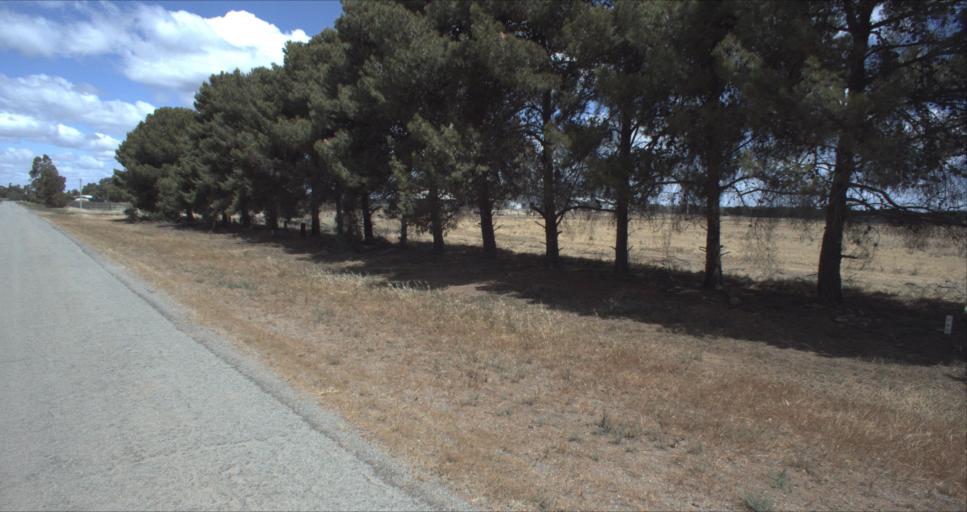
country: AU
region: New South Wales
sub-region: Murrumbidgee Shire
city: Darlington Point
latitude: -34.5112
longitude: 146.1847
